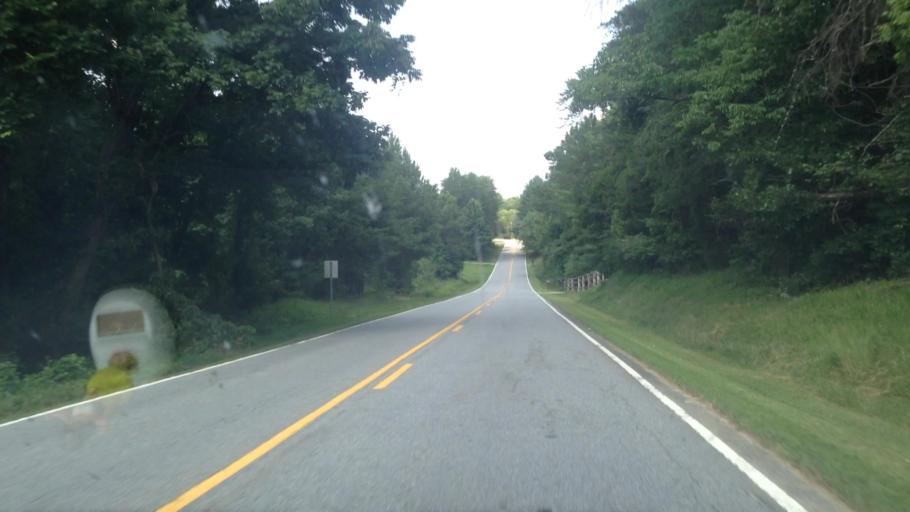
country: US
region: North Carolina
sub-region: Stokes County
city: Walnut Cove
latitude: 36.2434
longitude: -80.1004
